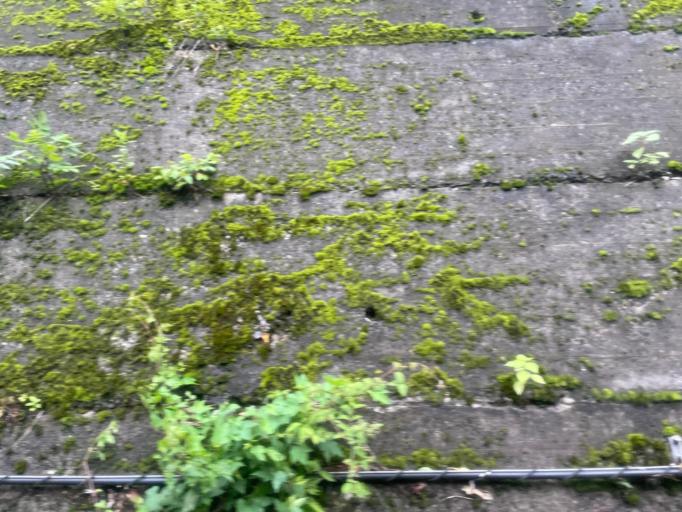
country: JP
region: Gunma
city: Numata
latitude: 36.7225
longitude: 138.9837
